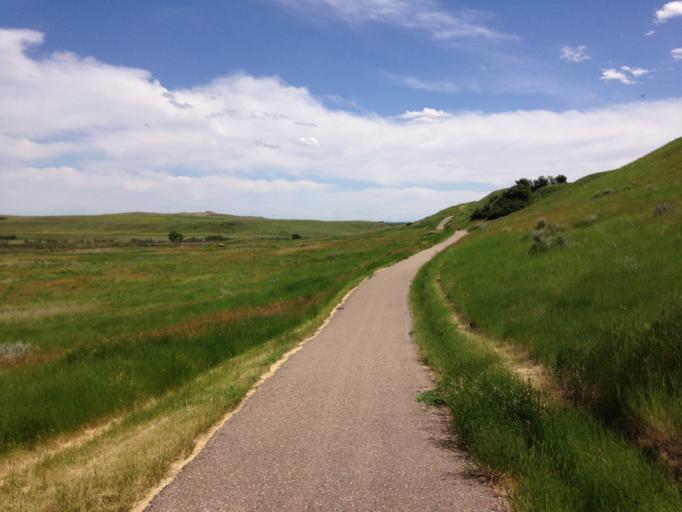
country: CA
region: Alberta
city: Medicine Hat
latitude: 50.0035
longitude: -110.6232
